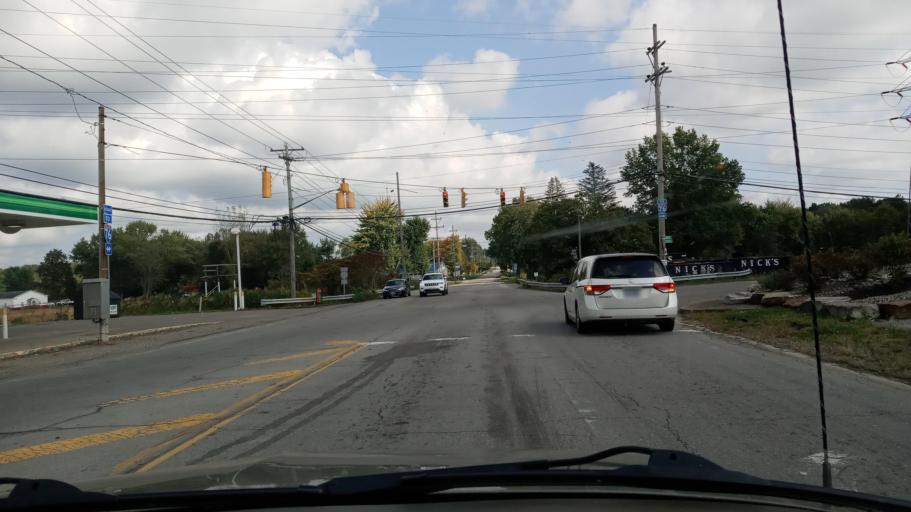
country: US
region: Ohio
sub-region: Summit County
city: Norton
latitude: 41.0549
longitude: -81.6096
